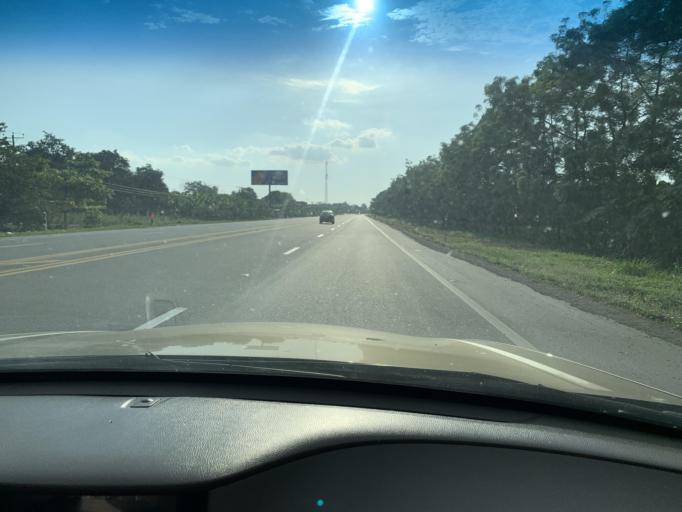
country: EC
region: Guayas
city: Coronel Marcelino Mariduena
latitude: -2.2796
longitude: -79.5248
